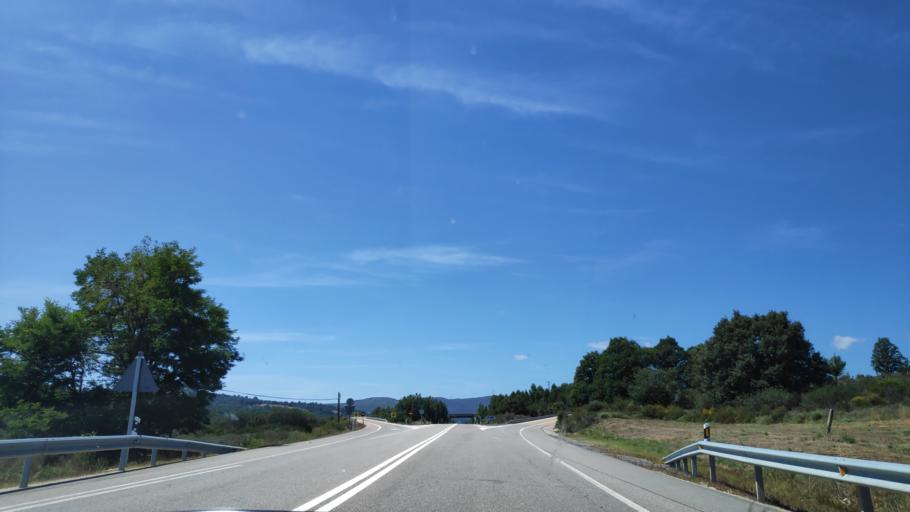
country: ES
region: Castille and Leon
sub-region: Provincia de Zamora
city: Puebla de Sanabria
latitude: 42.0576
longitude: -6.6629
